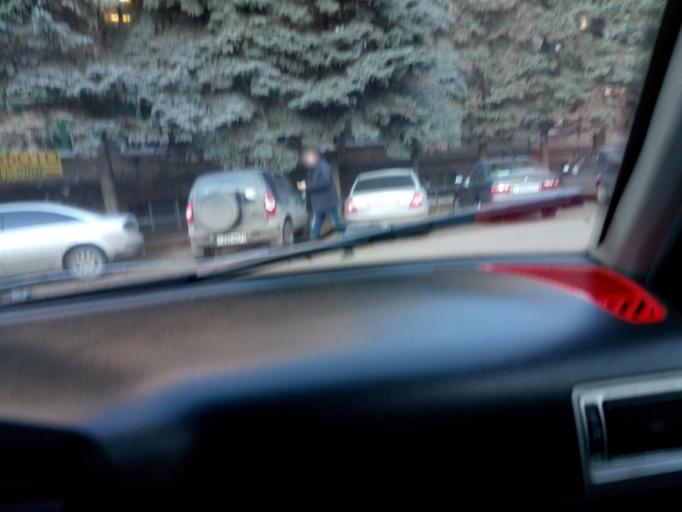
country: RU
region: Tula
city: Mendeleyevskiy
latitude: 54.1718
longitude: 37.5739
